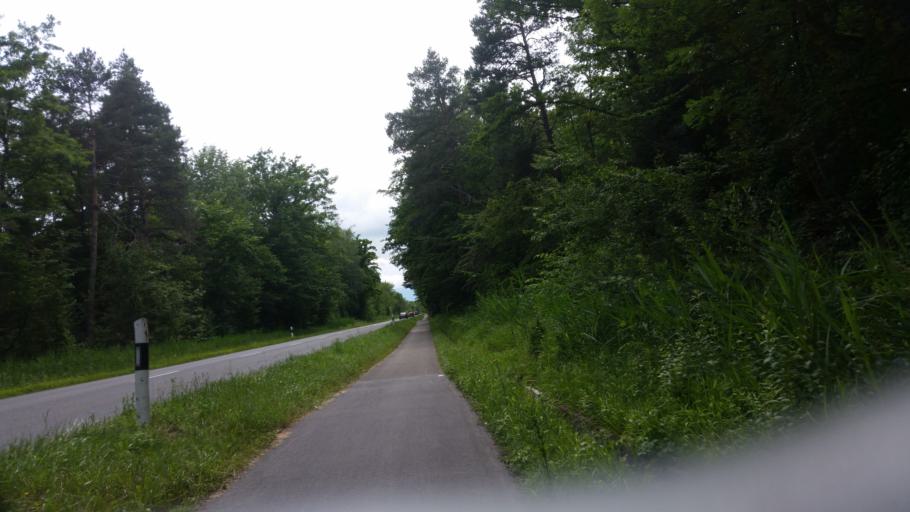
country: CH
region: Vaud
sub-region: Jura-Nord vaudois District
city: Yverdon-les-Bains
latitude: 46.7874
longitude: 6.6718
